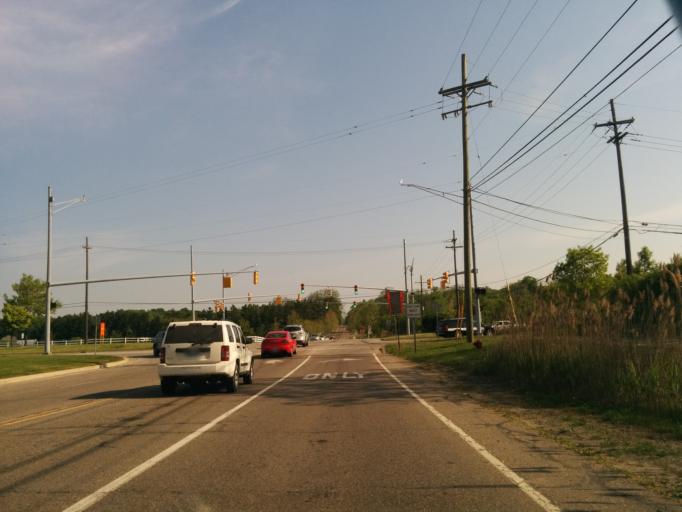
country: US
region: Michigan
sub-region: Oakland County
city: Novi
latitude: 42.4956
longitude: -83.4566
